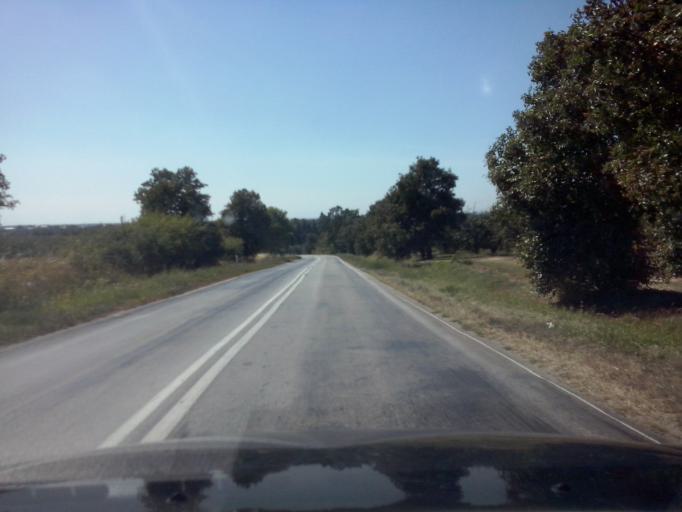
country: PL
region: Swietokrzyskie
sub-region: Powiat staszowski
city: Szydlow
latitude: 50.6018
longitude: 21.0088
